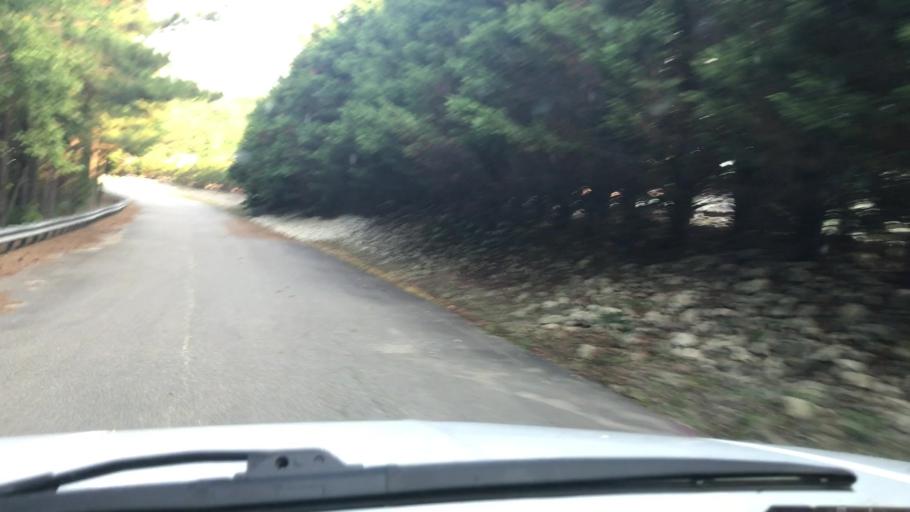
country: US
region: Virginia
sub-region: Henrico County
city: Short Pump
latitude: 37.5974
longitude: -77.7116
